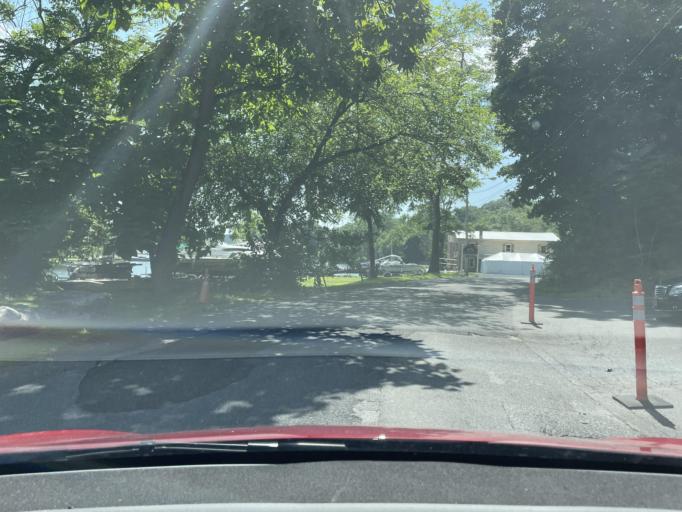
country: US
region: New York
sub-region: Ulster County
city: Saugerties
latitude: 42.0709
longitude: -73.9449
